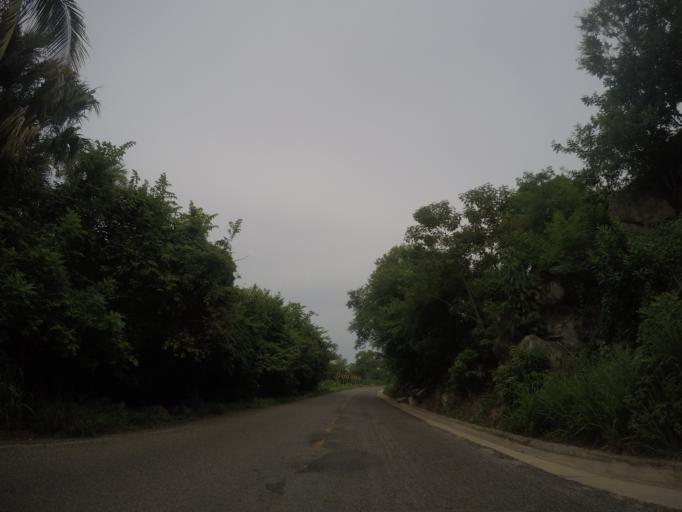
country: MX
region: Oaxaca
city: San Pedro Mixtepec
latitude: 15.9516
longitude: -97.1941
